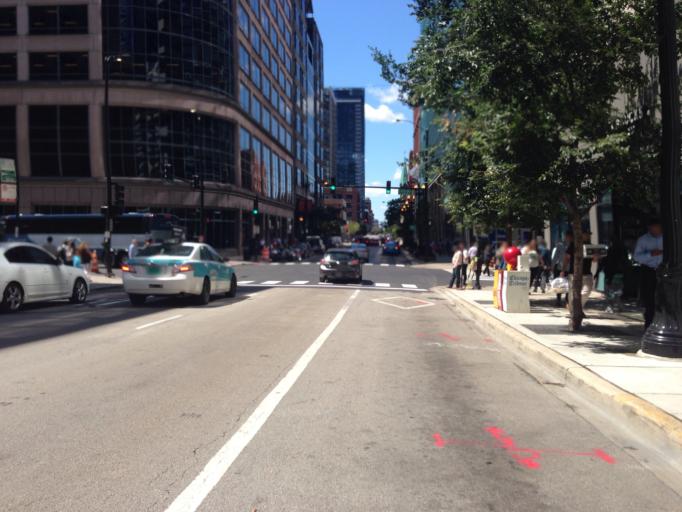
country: US
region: Illinois
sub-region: Cook County
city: Chicago
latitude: 41.8794
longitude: -87.6406
